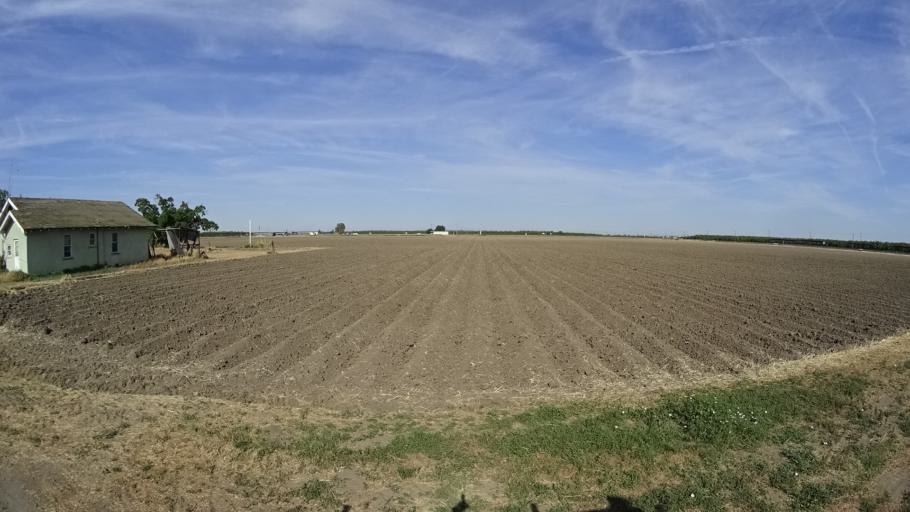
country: US
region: California
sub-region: Tulare County
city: Goshen
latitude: 36.3389
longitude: -119.4843
